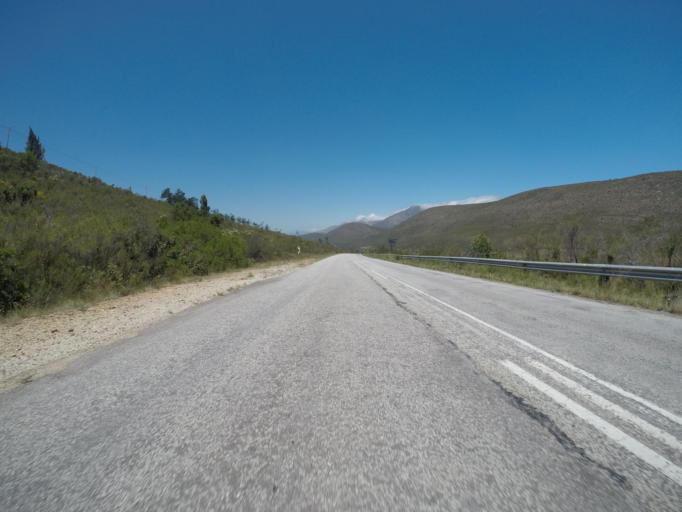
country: ZA
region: Eastern Cape
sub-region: Cacadu District Municipality
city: Kareedouw
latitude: -33.8587
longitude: 23.9944
